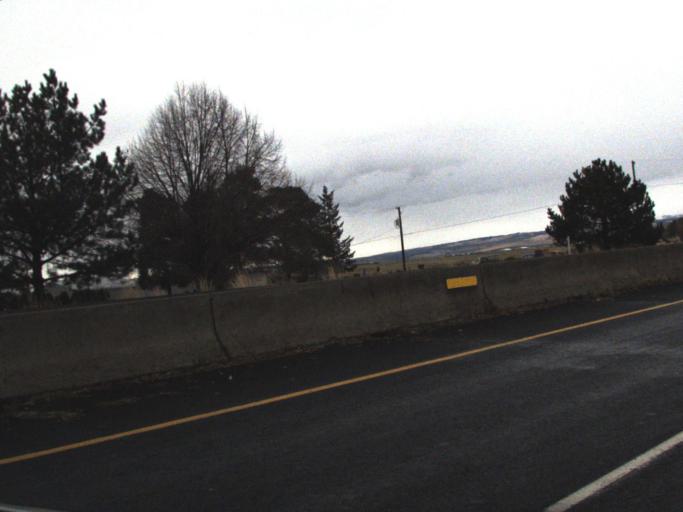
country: US
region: Washington
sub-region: Walla Walla County
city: Walla Walla
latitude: 46.0829
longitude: -118.3188
